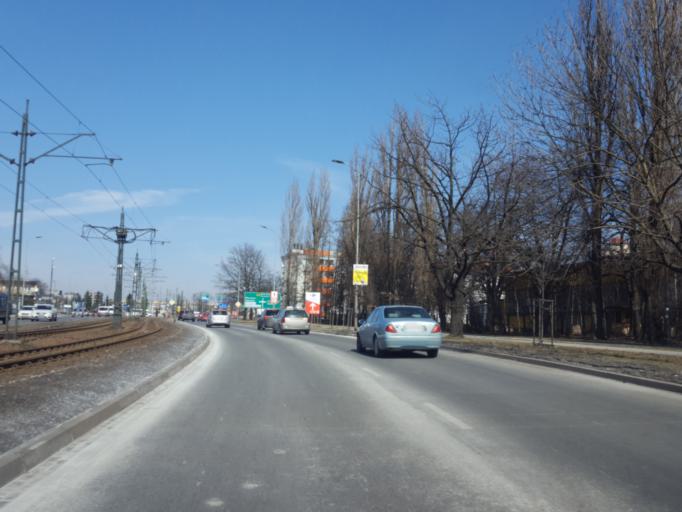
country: PL
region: Lesser Poland Voivodeship
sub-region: Krakow
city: Krakow
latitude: 50.0708
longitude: 20.0160
